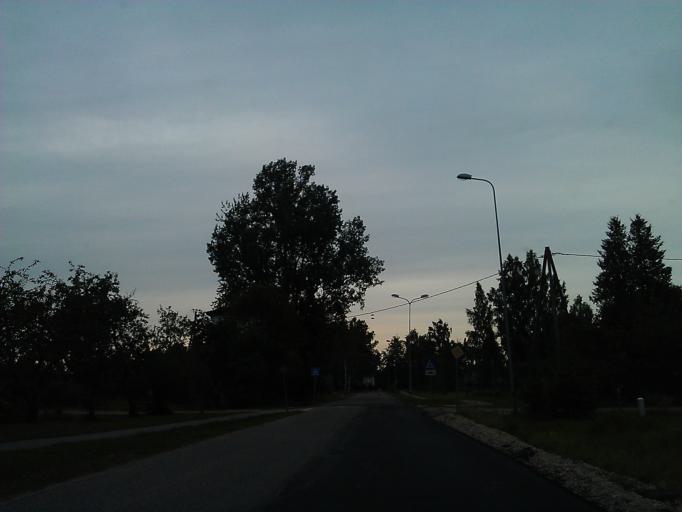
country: LV
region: Amatas Novads
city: Drabesi
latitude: 57.2052
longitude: 25.1658
